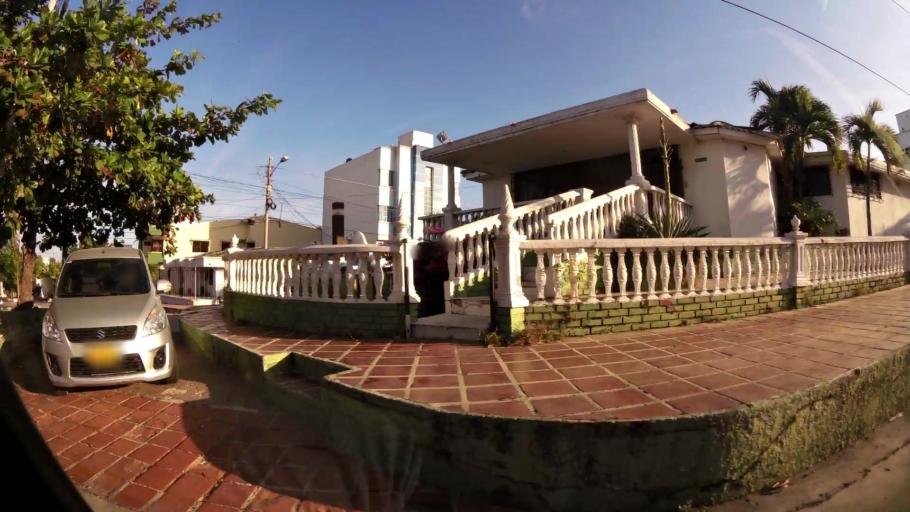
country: CO
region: Atlantico
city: Barranquilla
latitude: 10.9852
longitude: -74.8044
